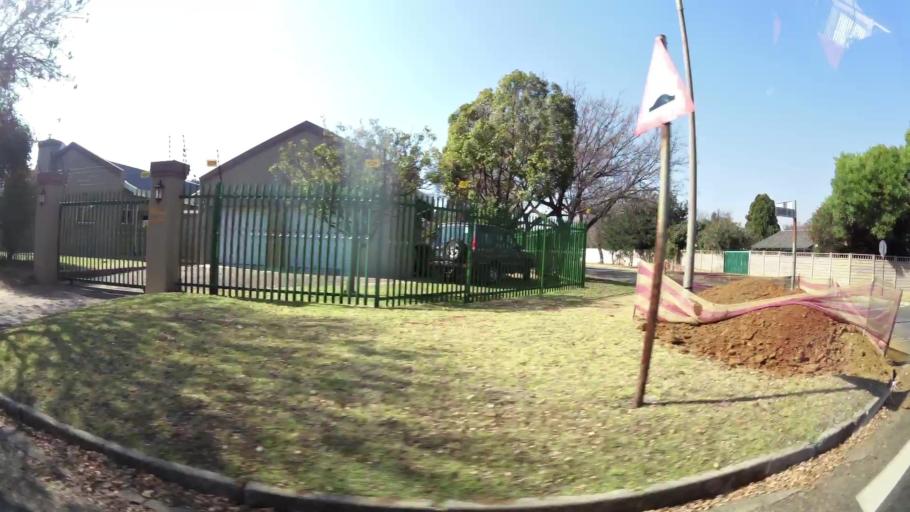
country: ZA
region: Gauteng
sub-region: Ekurhuleni Metropolitan Municipality
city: Boksburg
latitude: -26.1577
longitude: 28.2649
